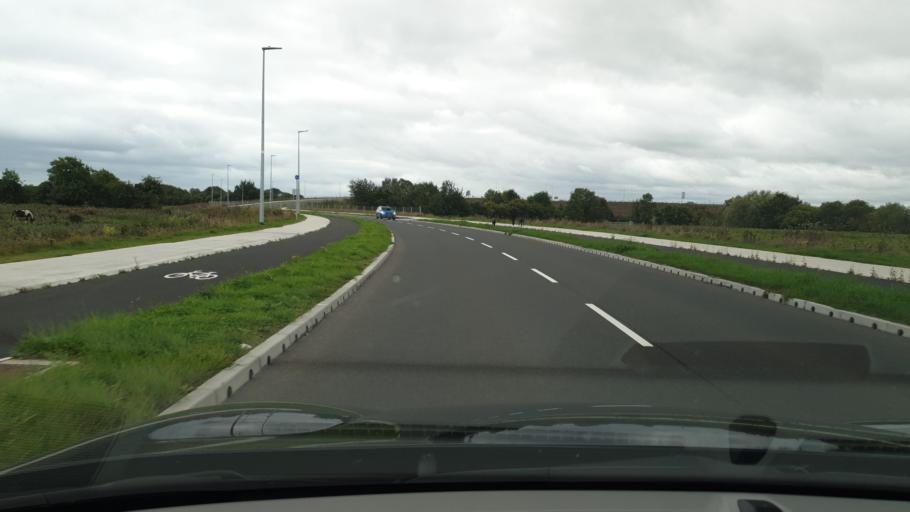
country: IE
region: Leinster
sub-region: Kildare
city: Sallins
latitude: 53.2515
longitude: -6.6759
